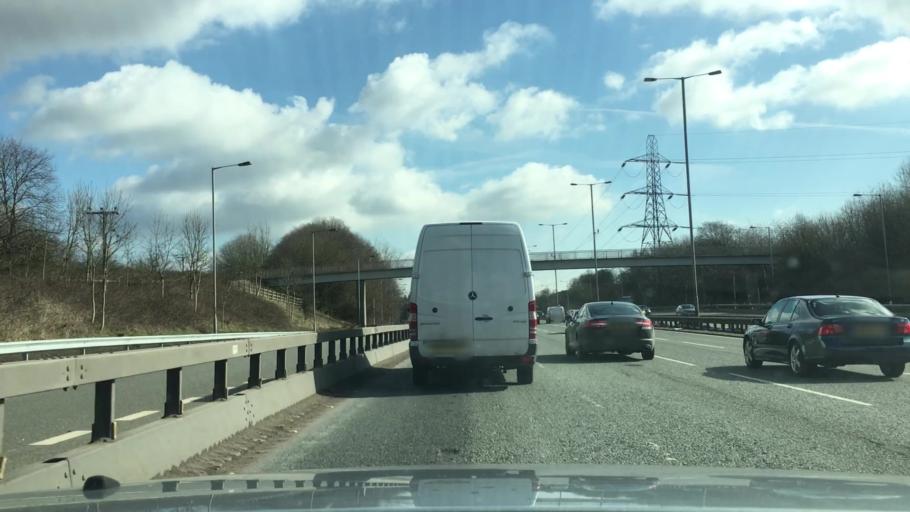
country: GB
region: England
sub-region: Borough of Bury
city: Whitefield
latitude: 53.5373
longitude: -2.2987
